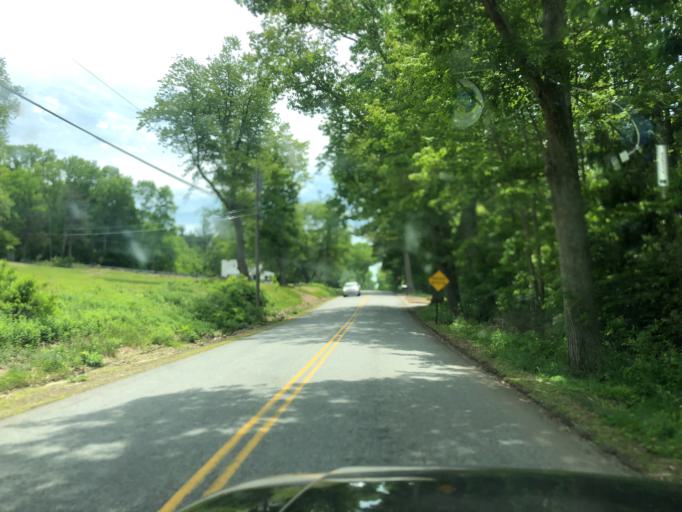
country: US
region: Connecticut
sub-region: Windham County
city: North Grosvenor Dale
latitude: 41.9833
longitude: -71.8923
